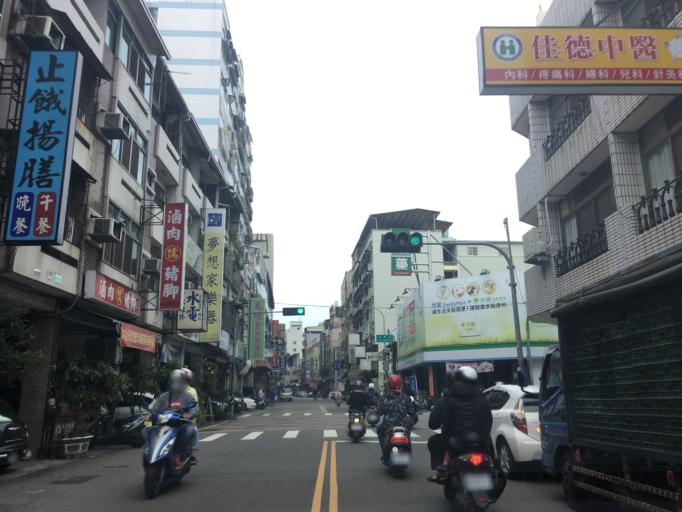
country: TW
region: Taiwan
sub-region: Taichung City
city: Taichung
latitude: 24.1732
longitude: 120.6635
